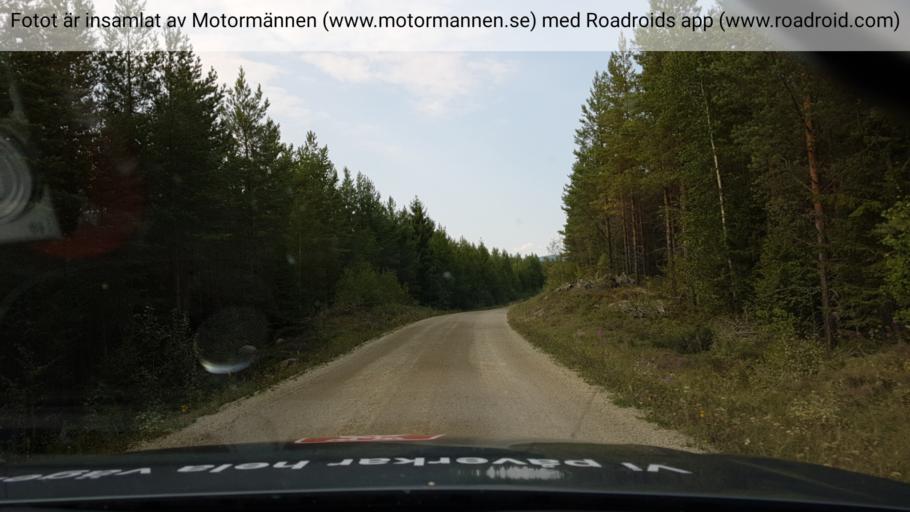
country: SE
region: Jaemtland
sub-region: Braecke Kommun
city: Braecke
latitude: 62.4694
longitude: 14.9150
